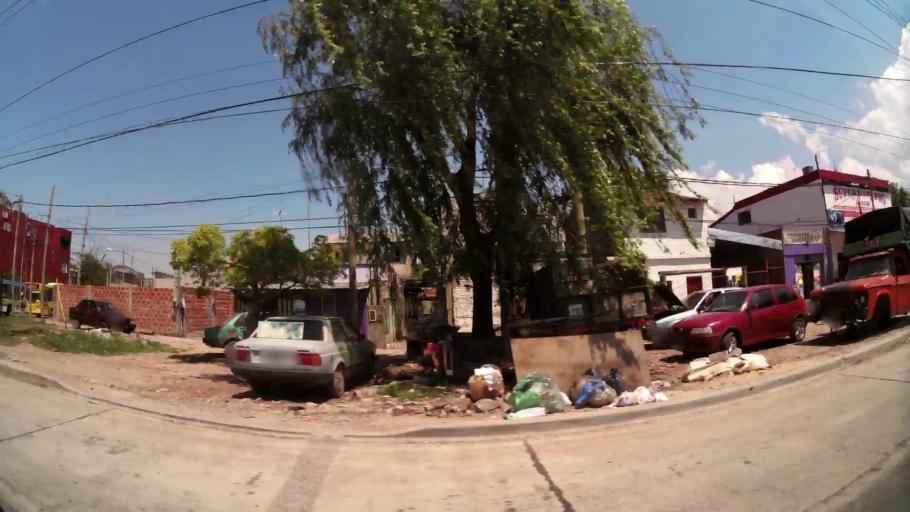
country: AR
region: Buenos Aires
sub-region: Partido de Tigre
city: Tigre
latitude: -34.4428
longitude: -58.5909
